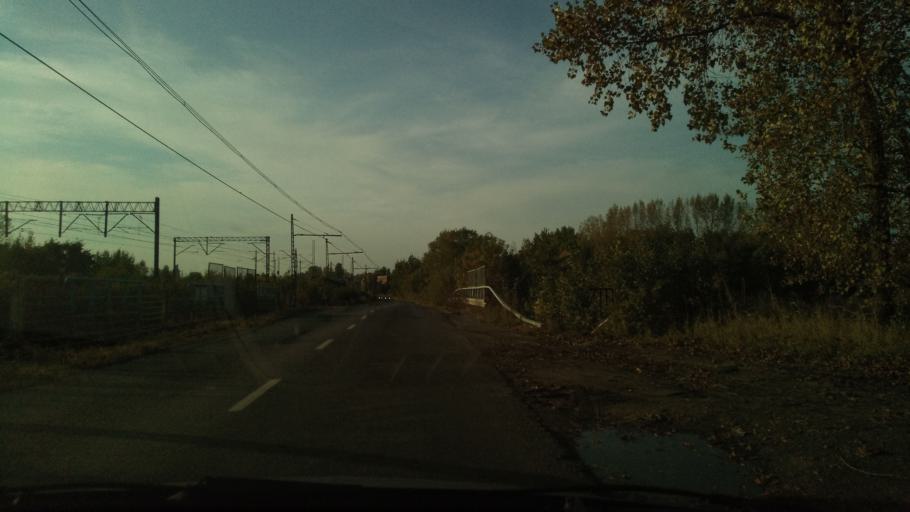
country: PL
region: Silesian Voivodeship
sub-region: Sosnowiec
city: Sosnowiec
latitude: 50.2555
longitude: 19.1191
